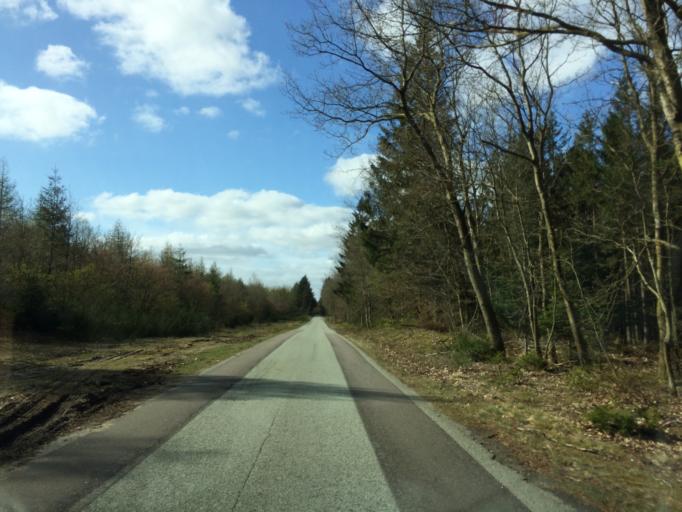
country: DK
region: Central Jutland
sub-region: Holstebro Kommune
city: Ulfborg
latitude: 56.2088
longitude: 8.4518
